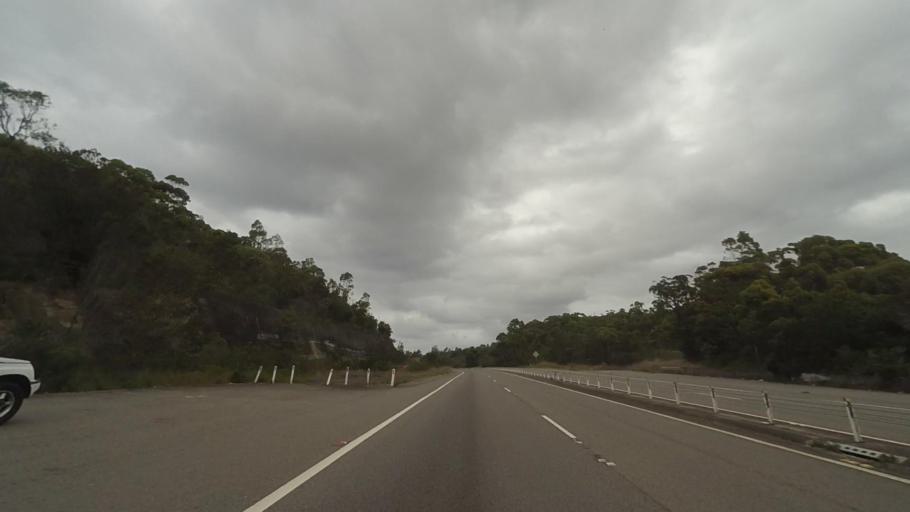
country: AU
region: New South Wales
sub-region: Lake Macquarie Shire
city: Arcadia vale
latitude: -33.1171
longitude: 151.6288
